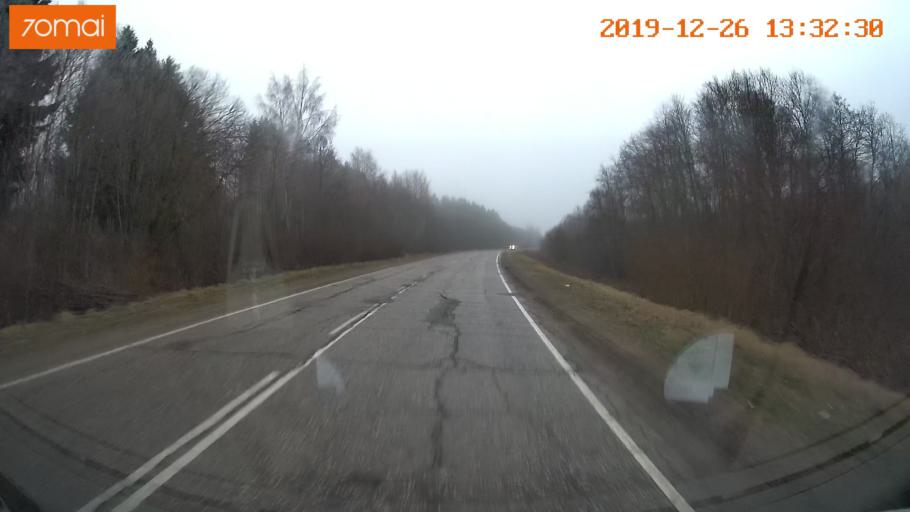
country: RU
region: Vologda
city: Sheksna
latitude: 58.8279
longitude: 38.2925
